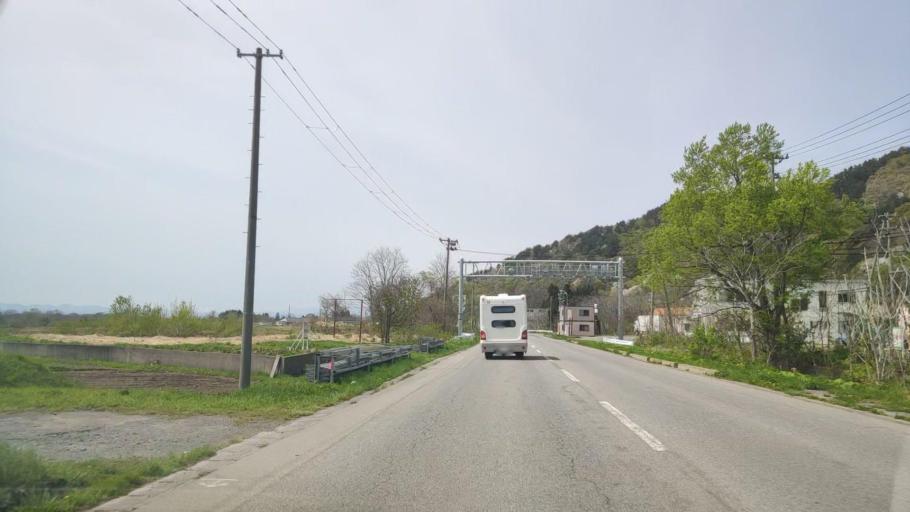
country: JP
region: Aomori
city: Aomori Shi
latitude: 40.8284
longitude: 140.8522
